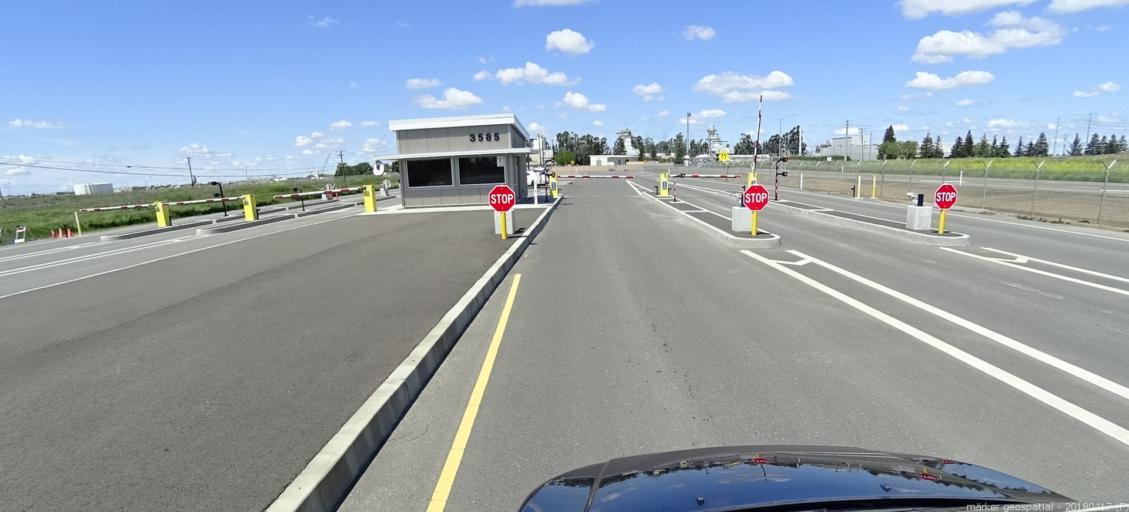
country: US
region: California
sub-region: Sacramento County
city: Laguna
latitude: 38.4425
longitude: -121.4633
